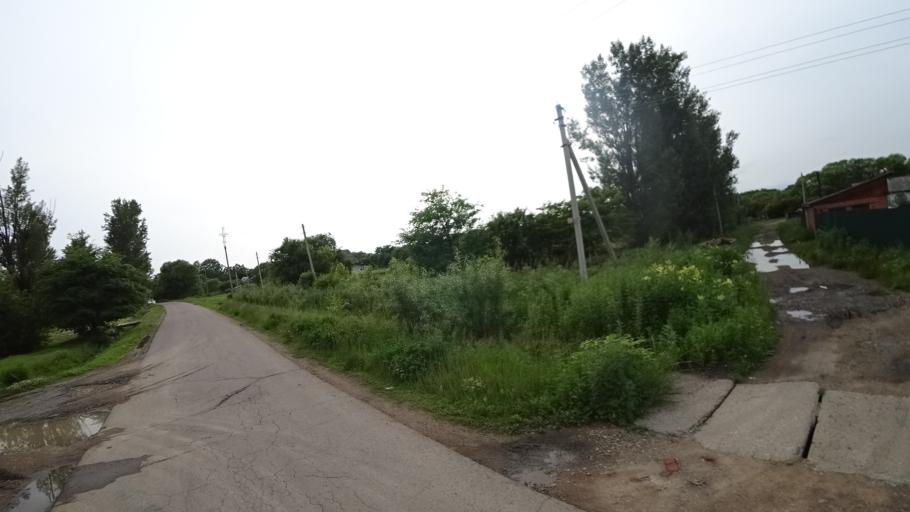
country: RU
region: Primorskiy
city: Novosysoyevka
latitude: 44.2466
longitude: 133.3728
